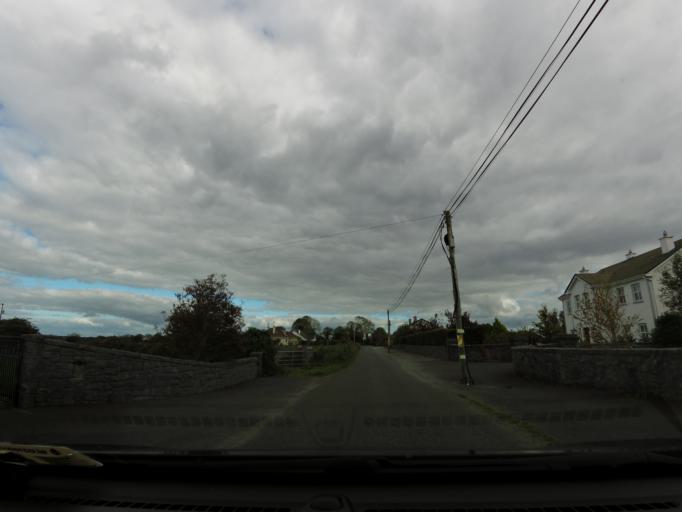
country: IE
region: Connaught
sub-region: County Galway
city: Moycullen
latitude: 53.3423
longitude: -9.1599
